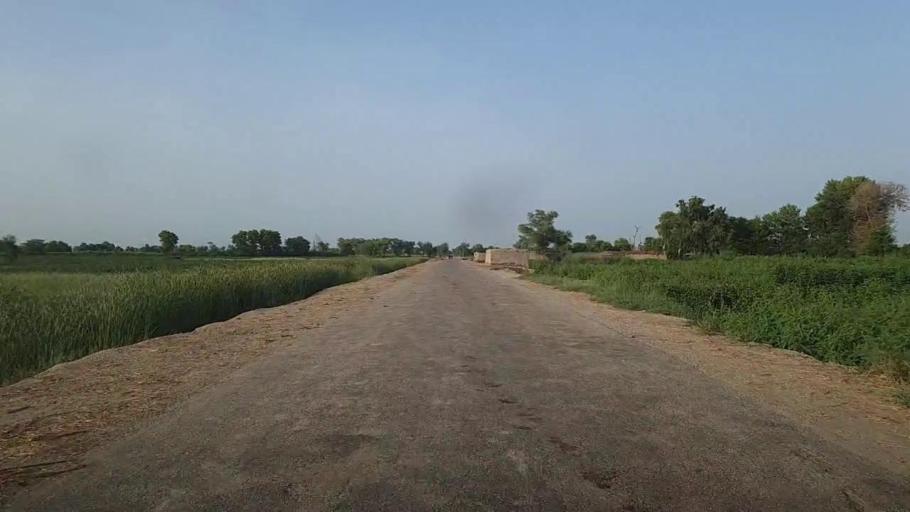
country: PK
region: Sindh
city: Ubauro
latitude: 28.1210
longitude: 69.8261
